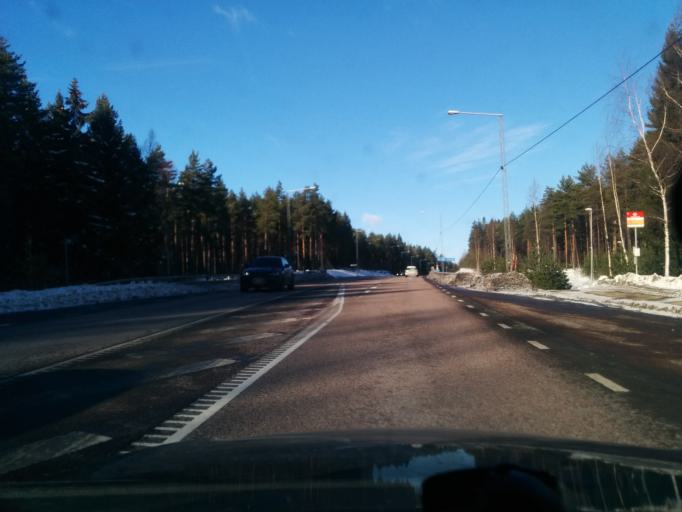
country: SE
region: Stockholm
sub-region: Vallentuna Kommun
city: Vallentuna
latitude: 59.4985
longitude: 18.1008
